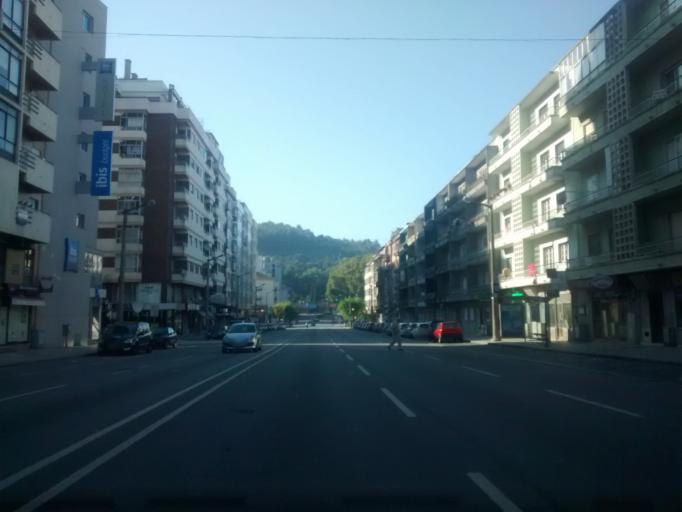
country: PT
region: Braga
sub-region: Braga
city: Braga
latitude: 41.5454
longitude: -8.4195
